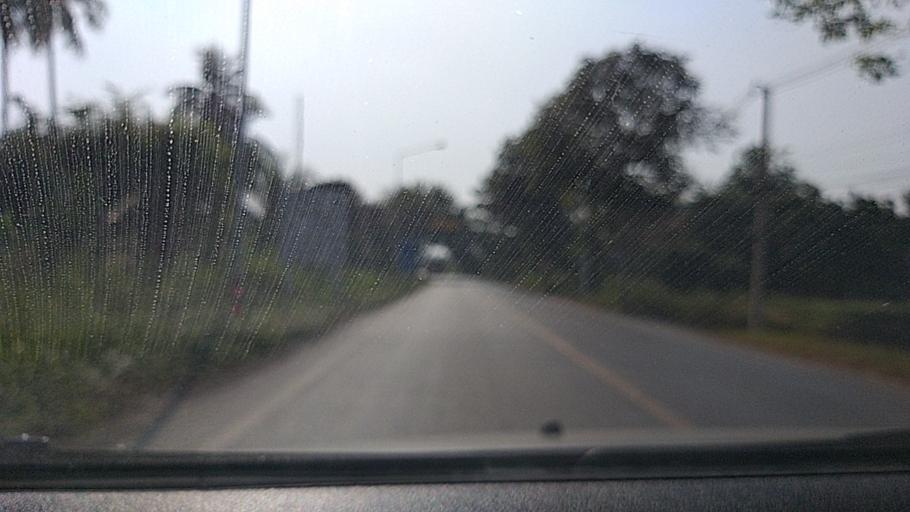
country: TH
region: Ang Thong
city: Chaiyo
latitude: 14.7197
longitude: 100.4455
